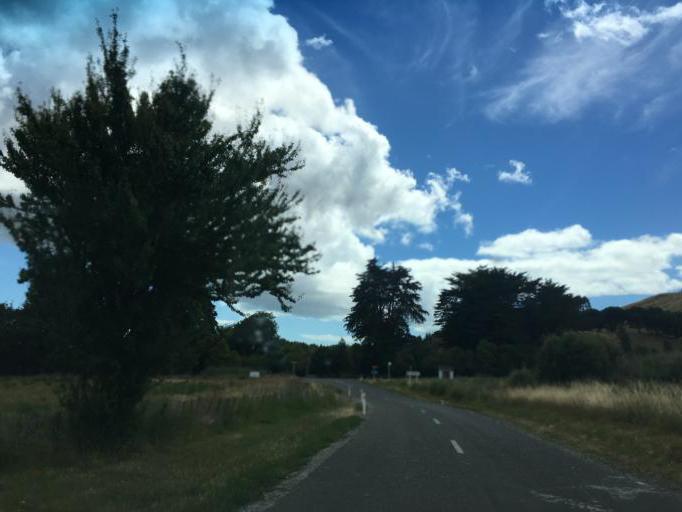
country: NZ
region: Hawke's Bay
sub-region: Hastings District
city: Hastings
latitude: -39.7201
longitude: 176.9279
